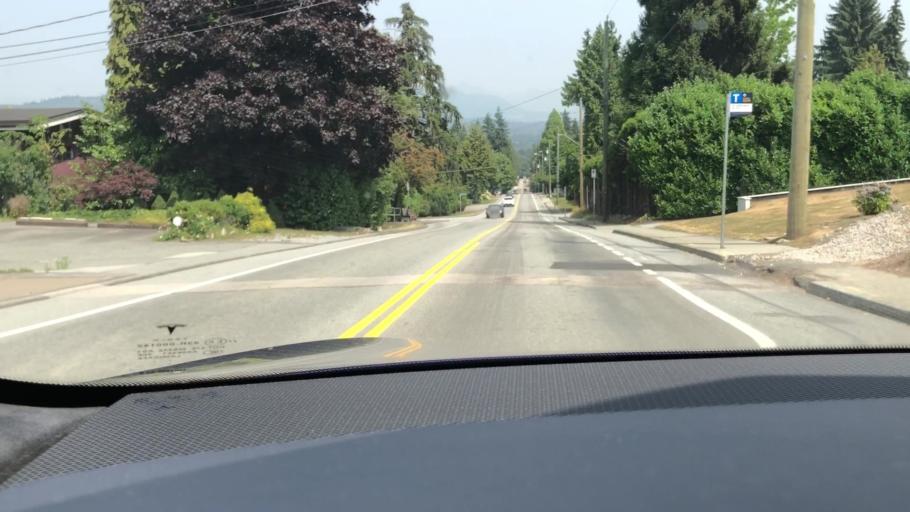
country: CA
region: British Columbia
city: Burnaby
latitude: 49.2307
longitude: -122.9630
